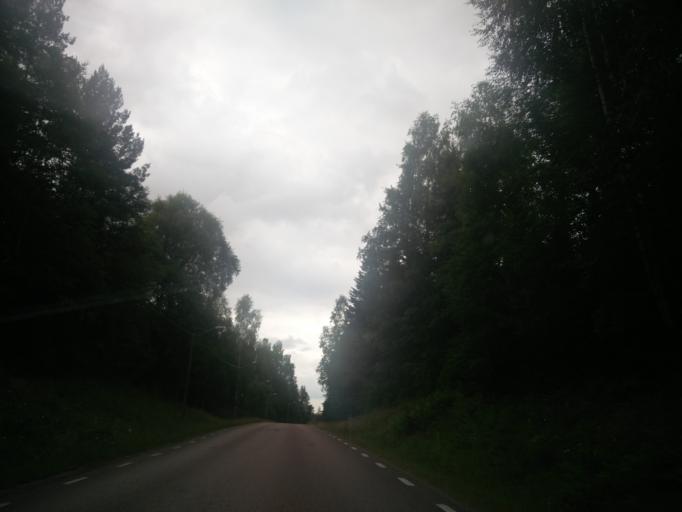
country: SE
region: Vaermland
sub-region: Arvika Kommun
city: Arvika
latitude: 59.8940
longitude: 12.6348
